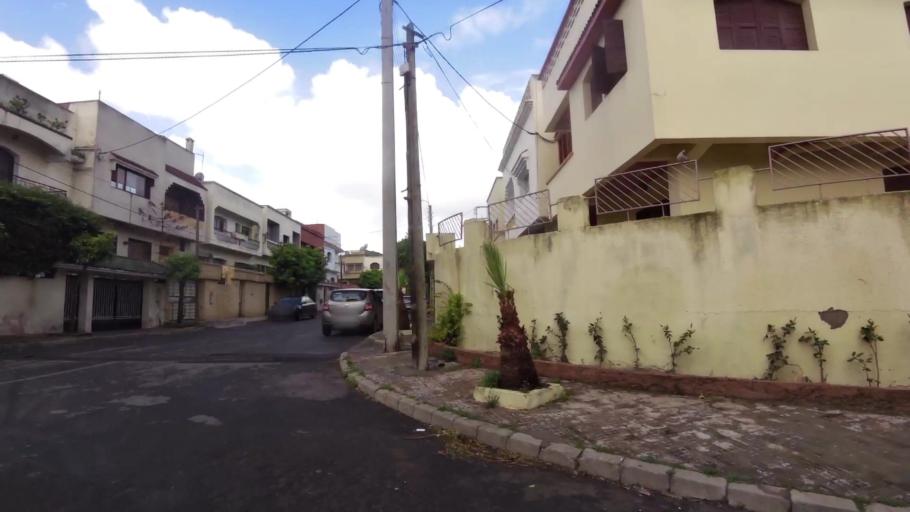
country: MA
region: Grand Casablanca
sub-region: Casablanca
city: Casablanca
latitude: 33.5633
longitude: -7.6789
